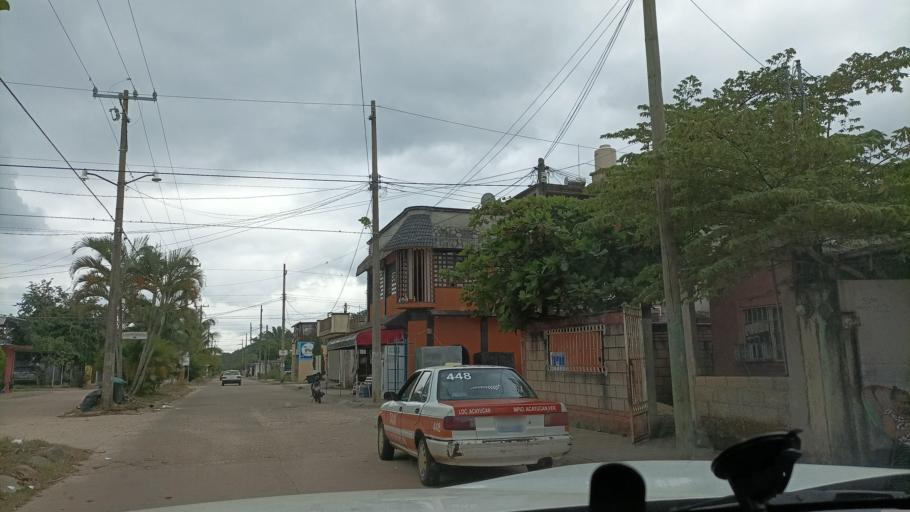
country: MX
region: Veracruz
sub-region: Soconusco
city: Fraccionamiento Santa Cruz
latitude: 17.9712
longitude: -94.8936
